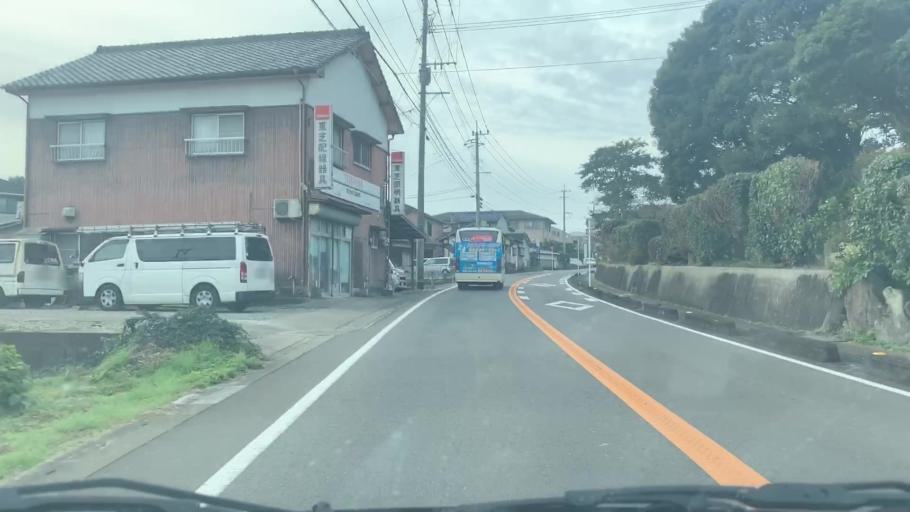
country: JP
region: Saga Prefecture
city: Ureshinomachi-shimojuku
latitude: 33.1215
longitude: 130.0021
